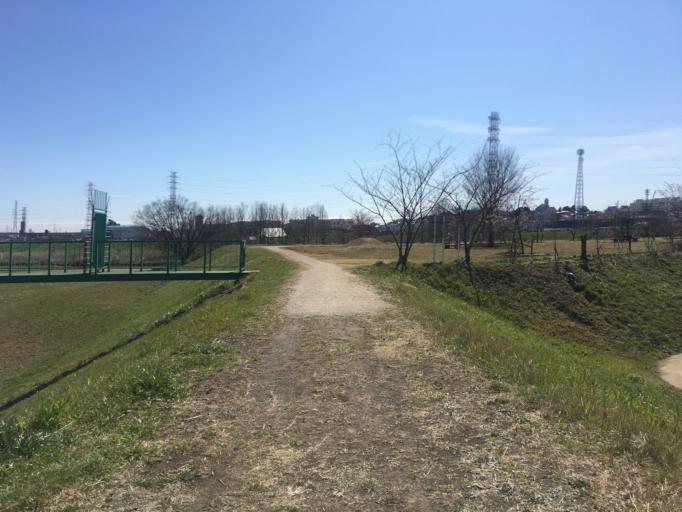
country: JP
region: Saitama
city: Asaka
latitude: 35.8139
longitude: 139.6099
